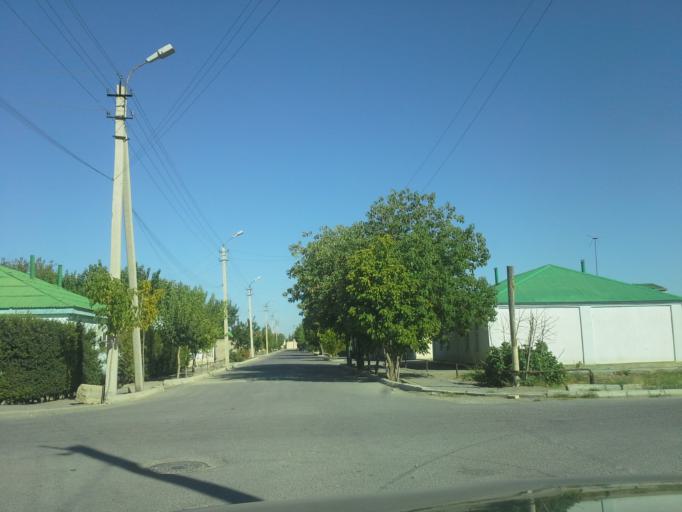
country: TM
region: Ahal
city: Abadan
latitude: 38.0716
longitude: 58.1538
